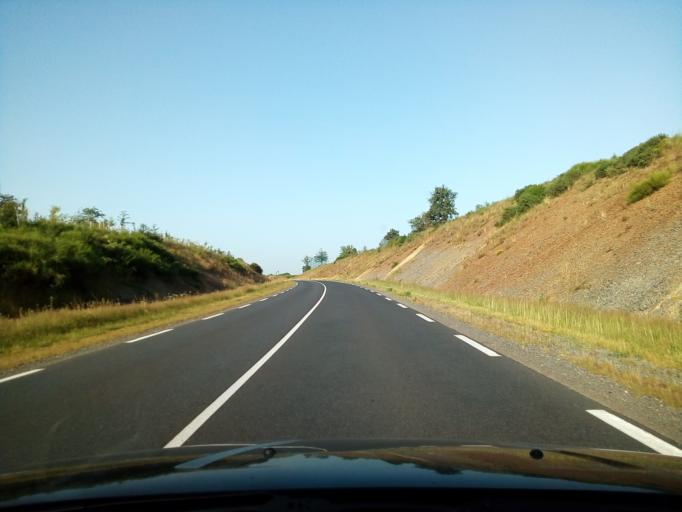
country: FR
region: Limousin
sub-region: Departement de la Haute-Vienne
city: Bussiere-Poitevine
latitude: 46.1153
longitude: 0.9015
